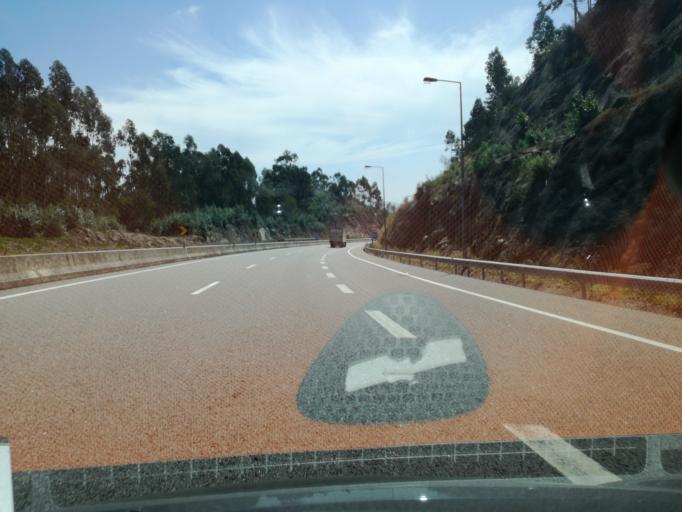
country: PT
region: Viana do Castelo
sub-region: Viana do Castelo
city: Meadela
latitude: 41.7416
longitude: -8.7937
